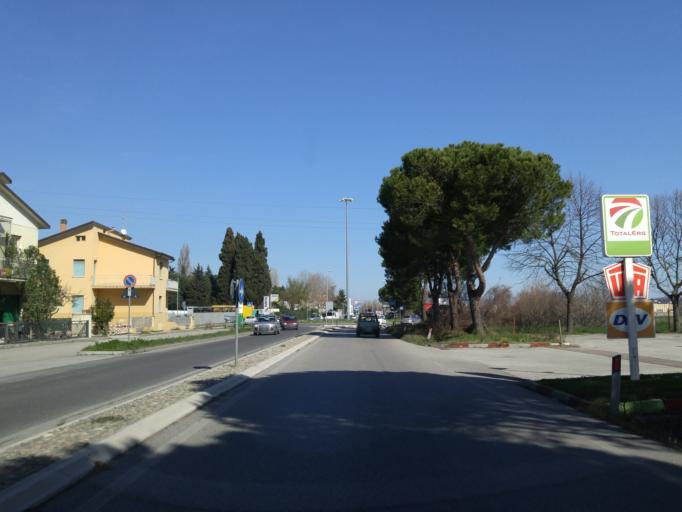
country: IT
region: Emilia-Romagna
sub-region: Provincia di Rimini
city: San Giovanni in Marignano
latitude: 43.9468
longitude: 12.7205
